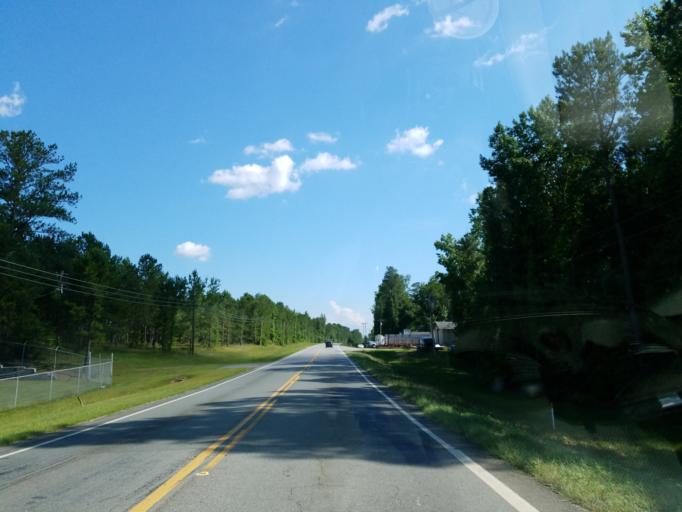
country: US
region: Georgia
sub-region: Crawford County
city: Roberta
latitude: 32.7032
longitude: -84.0095
